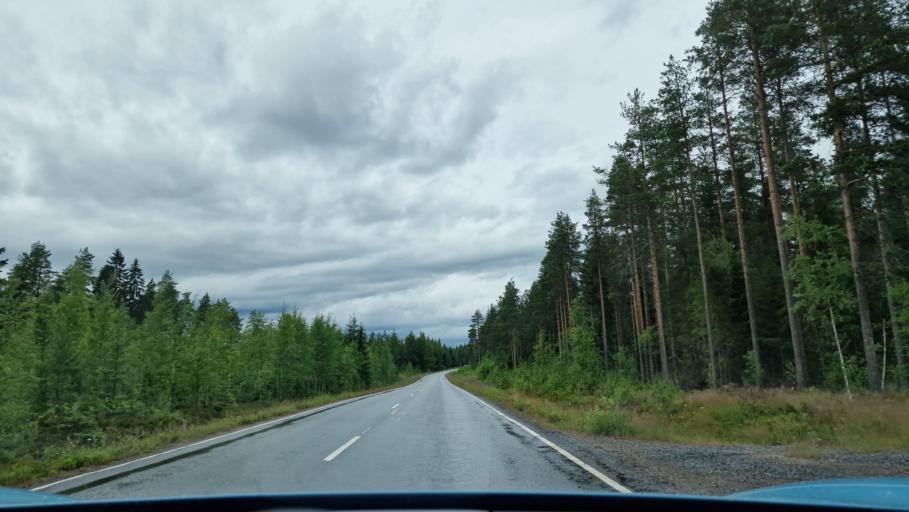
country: FI
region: Central Finland
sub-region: Saarijaervi-Viitasaari
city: Pylkoenmaeki
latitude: 62.6758
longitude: 24.5062
